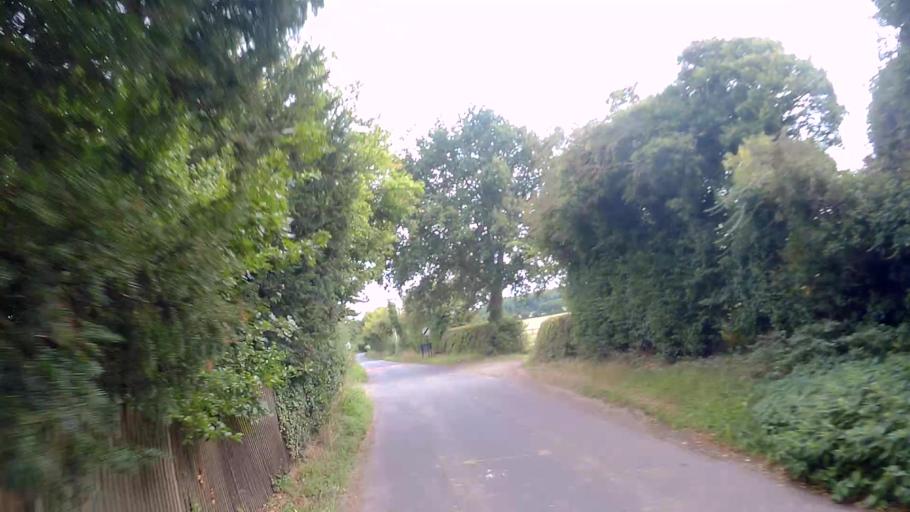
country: GB
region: England
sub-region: Hampshire
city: Overton
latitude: 51.1535
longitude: -1.2238
